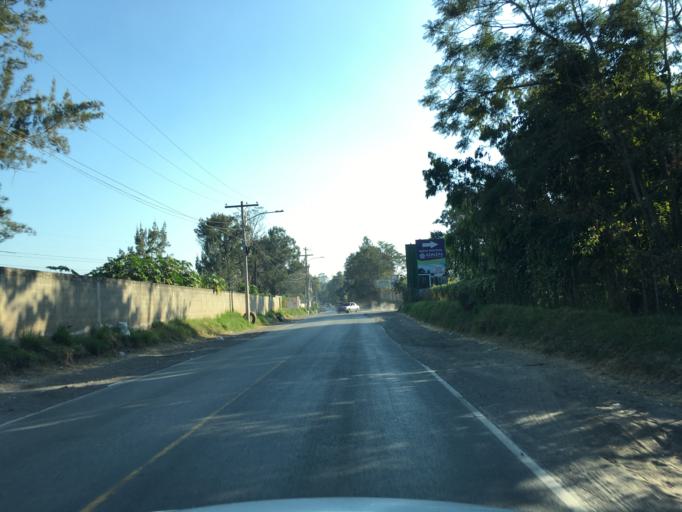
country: GT
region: Guatemala
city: Villa Nueva
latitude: 14.5279
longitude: -90.6169
